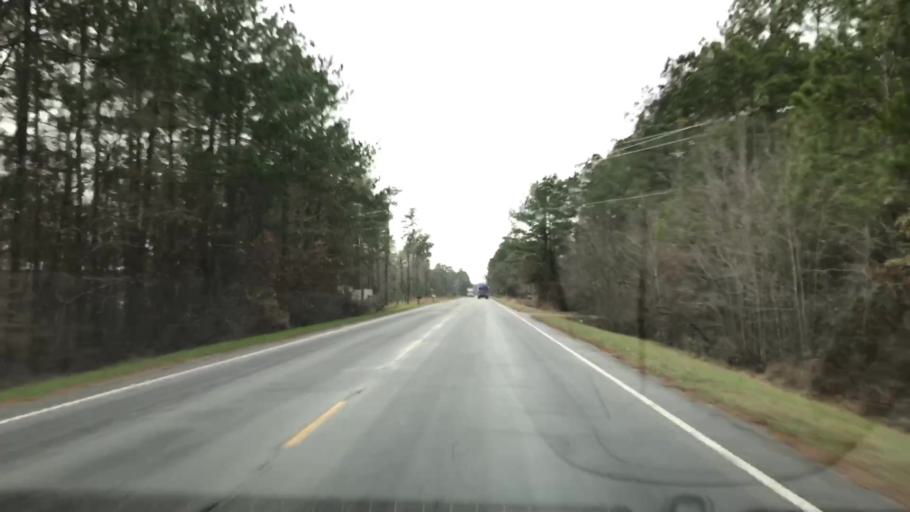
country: US
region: South Carolina
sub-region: Berkeley County
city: Saint Stephen
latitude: 33.2867
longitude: -79.8512
